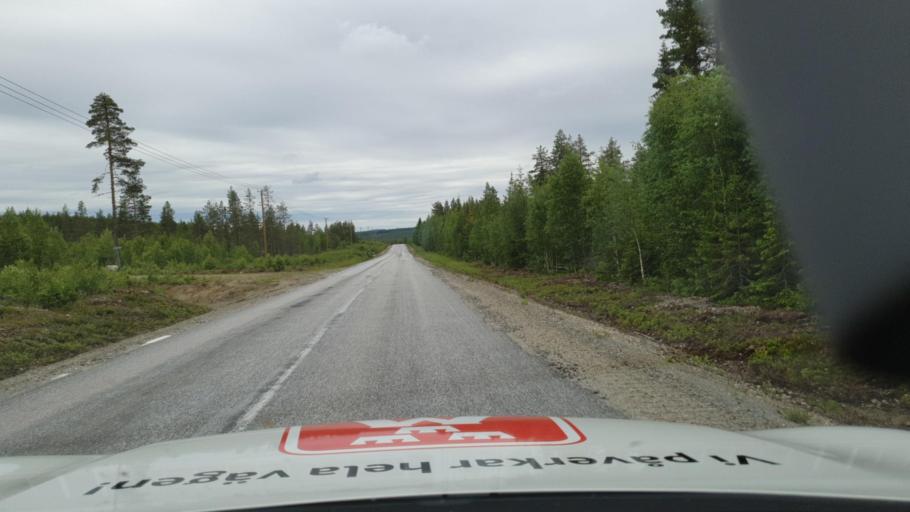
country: SE
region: Vaesterbotten
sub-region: Lycksele Kommun
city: Lycksele
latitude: 64.1120
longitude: 18.3635
